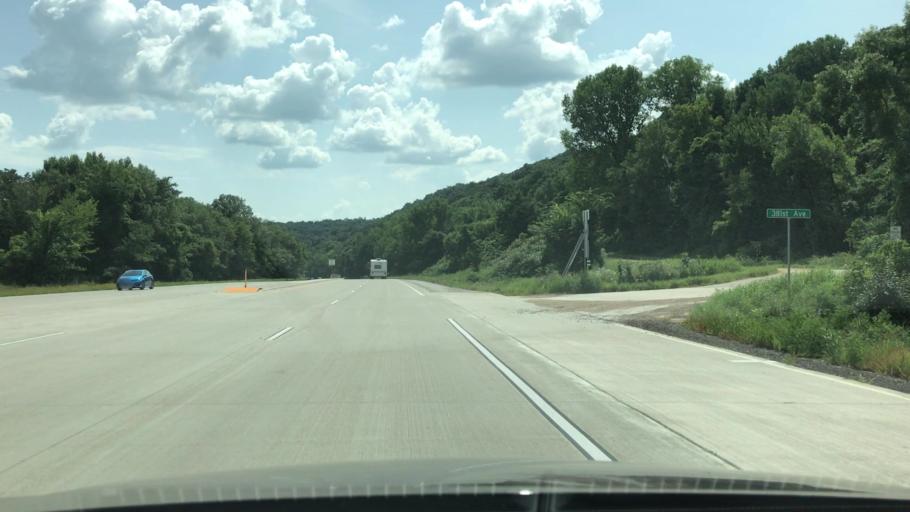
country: US
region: Minnesota
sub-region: Nicollet County
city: Saint Peter
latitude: 44.2713
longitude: -94.0199
